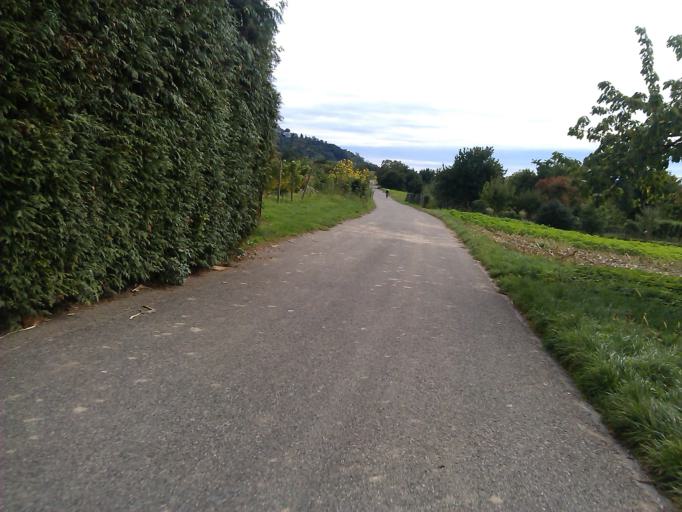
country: DE
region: Baden-Wuerttemberg
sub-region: Karlsruhe Region
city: Schriesheim
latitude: 49.4934
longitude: 8.6625
